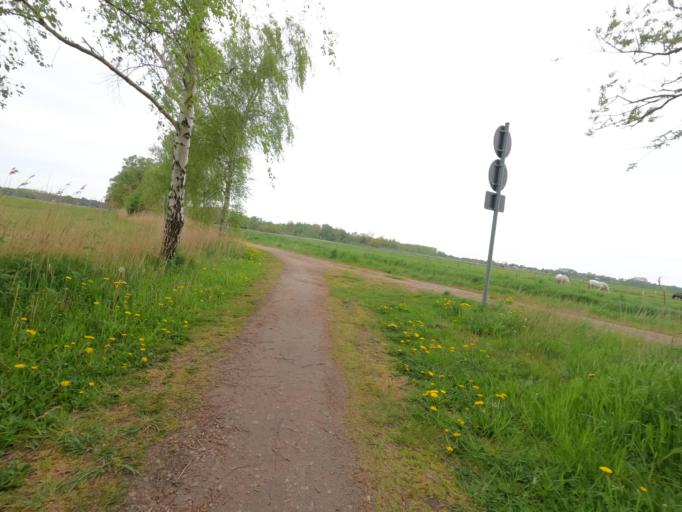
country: DE
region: Mecklenburg-Vorpommern
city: Ostseebad Dierhagen
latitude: 54.2962
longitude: 12.3566
